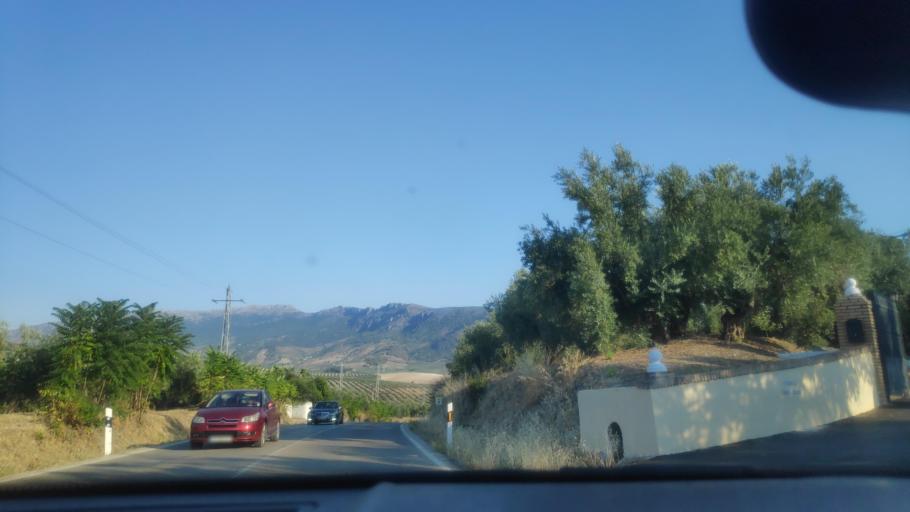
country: ES
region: Andalusia
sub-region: Provincia de Jaen
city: Jaen
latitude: 37.7295
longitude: -3.7632
